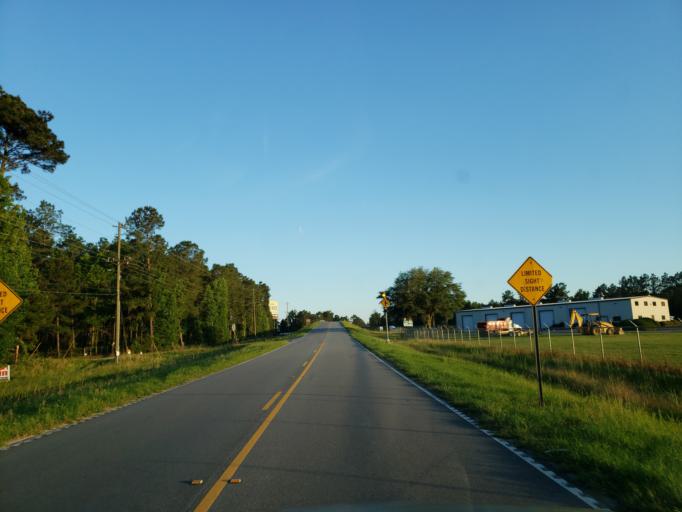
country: US
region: Georgia
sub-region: Lowndes County
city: Valdosta
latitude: 30.6972
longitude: -83.2398
